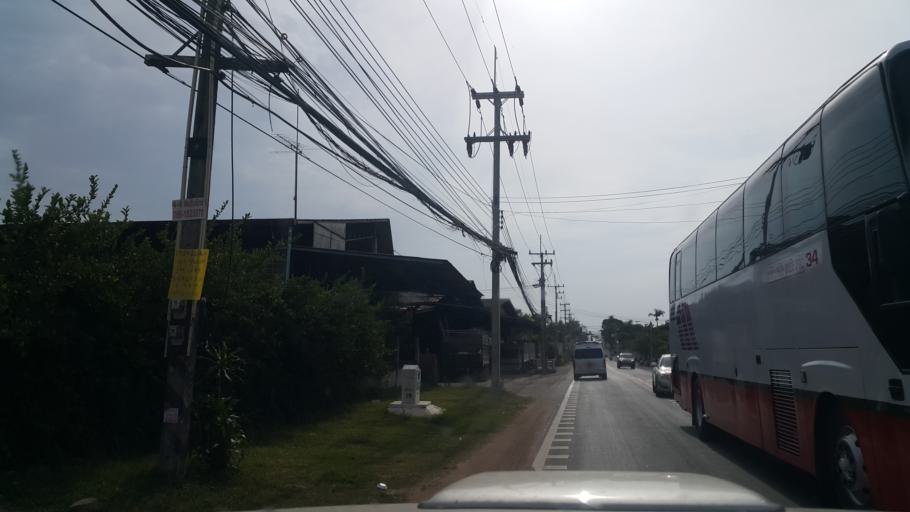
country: TH
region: Chon Buri
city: Sattahip
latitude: 12.7917
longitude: 100.9266
